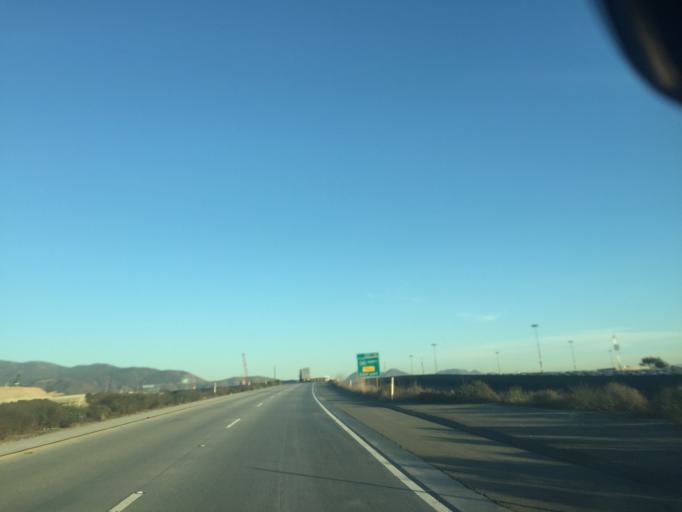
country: MX
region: Baja California
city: Tijuana
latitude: 32.5637
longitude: -116.9536
